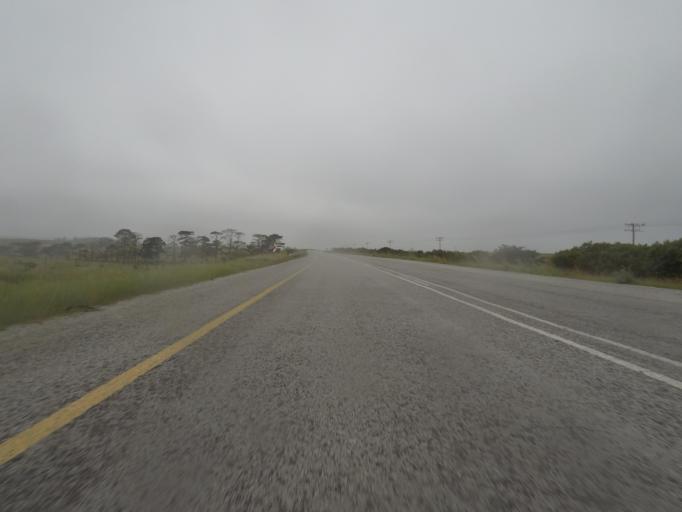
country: ZA
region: Eastern Cape
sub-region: Cacadu District Municipality
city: Grahamstown
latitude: -33.6421
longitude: 26.3335
